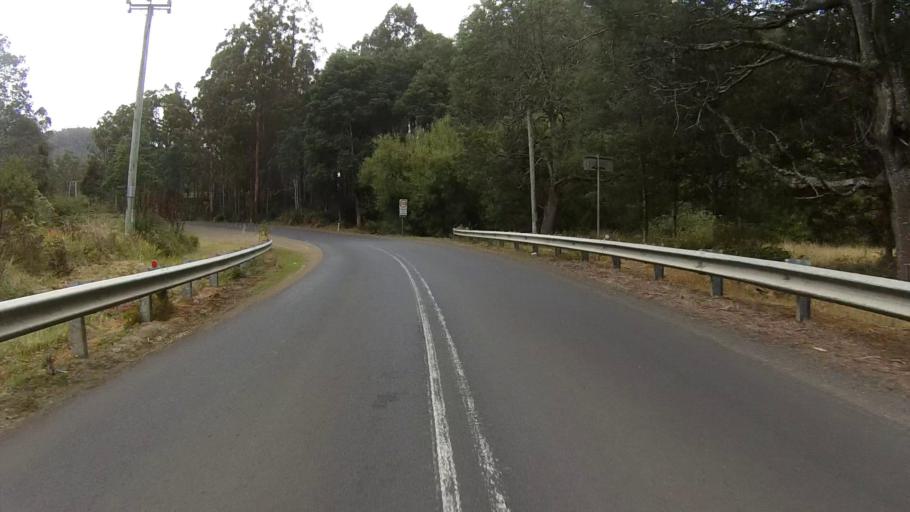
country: AU
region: Tasmania
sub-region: Huon Valley
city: Cygnet
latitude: -43.1415
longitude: 147.1536
